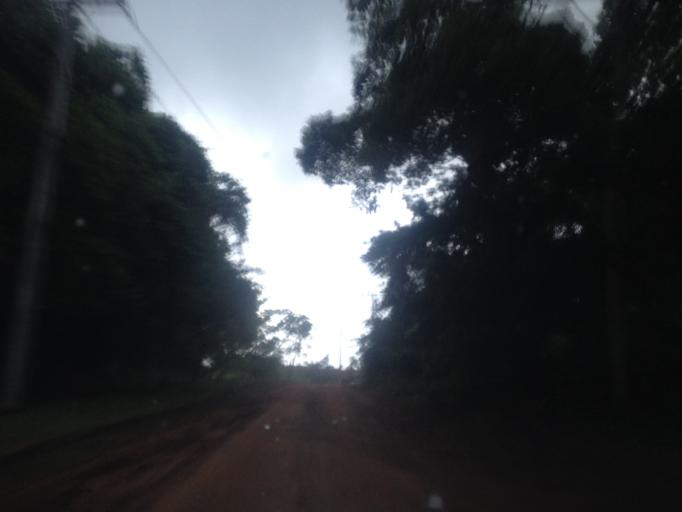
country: BR
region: Bahia
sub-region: Mata De Sao Joao
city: Mata de Sao Joao
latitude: -12.5731
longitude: -38.0242
